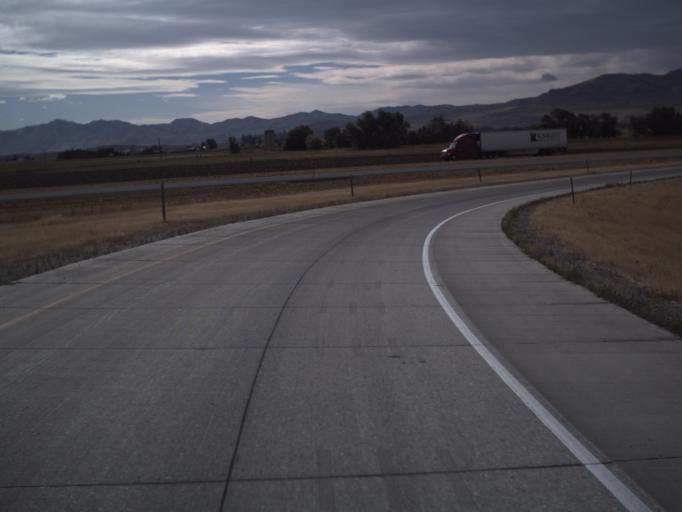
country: US
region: Utah
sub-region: Box Elder County
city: Tremonton
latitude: 41.7069
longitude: -112.1941
